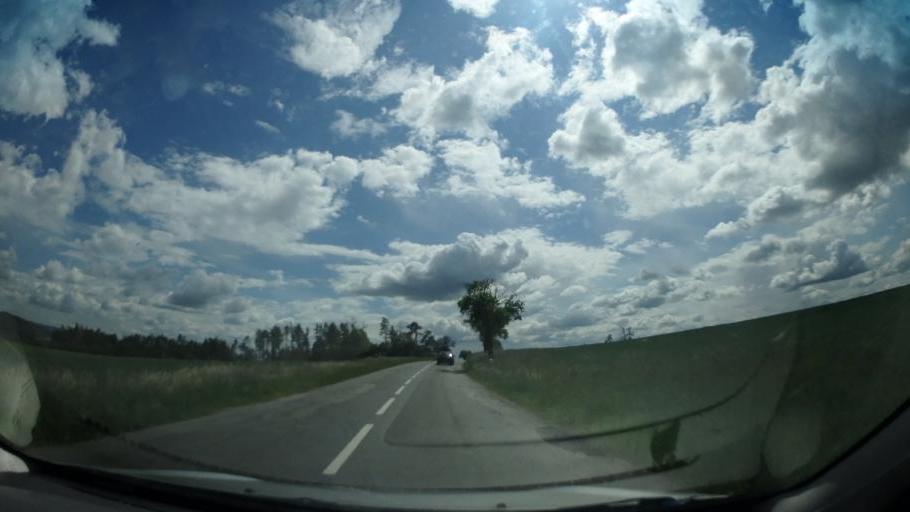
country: CZ
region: South Moravian
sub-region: Okres Blansko
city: Letovice
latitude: 49.5750
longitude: 16.5844
